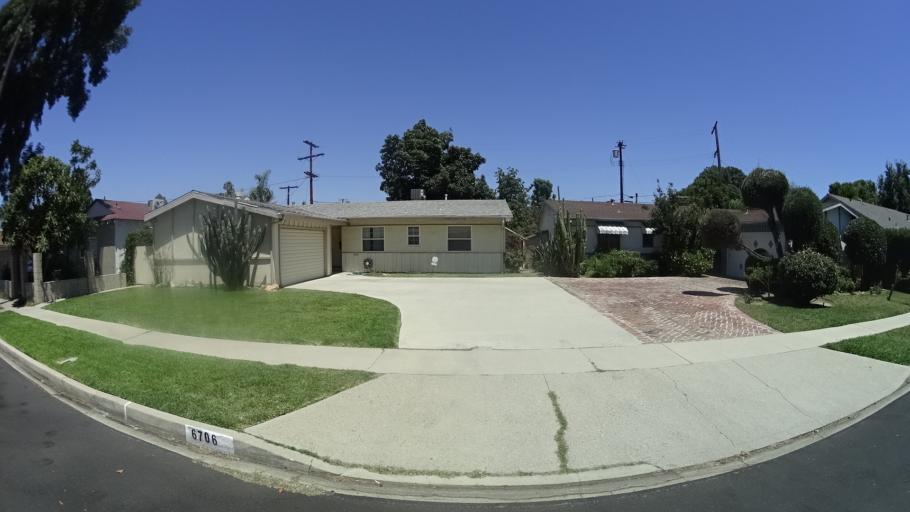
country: US
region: California
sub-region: Los Angeles County
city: Northridge
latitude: 34.1922
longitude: -118.5261
